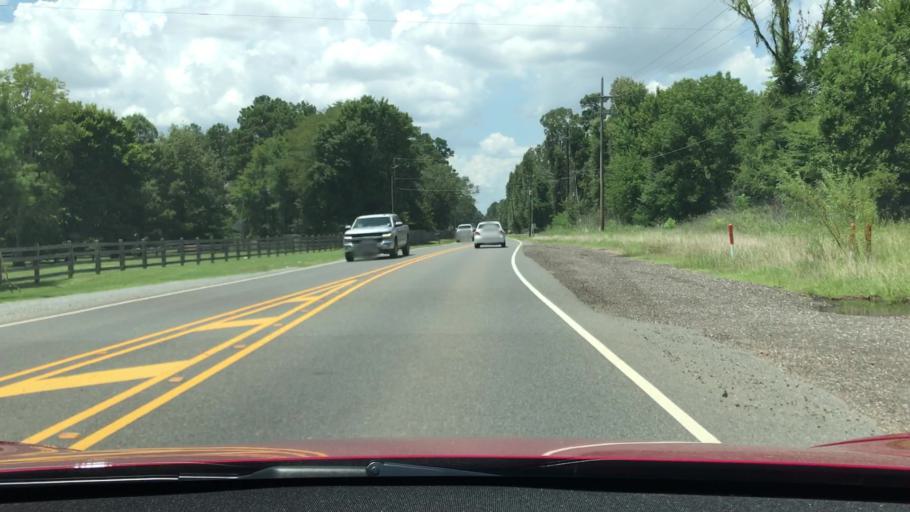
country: US
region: Louisiana
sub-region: De Soto Parish
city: Stonewall
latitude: 32.3649
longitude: -93.6932
